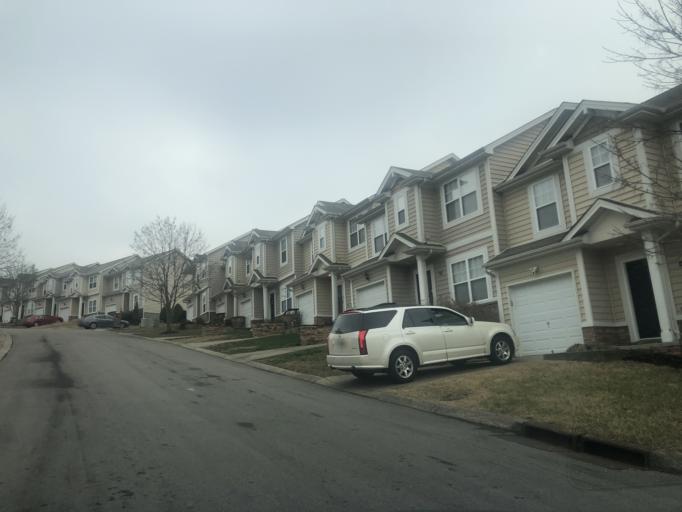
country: US
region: Tennessee
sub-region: Rutherford County
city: La Vergne
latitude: 36.0639
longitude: -86.6462
